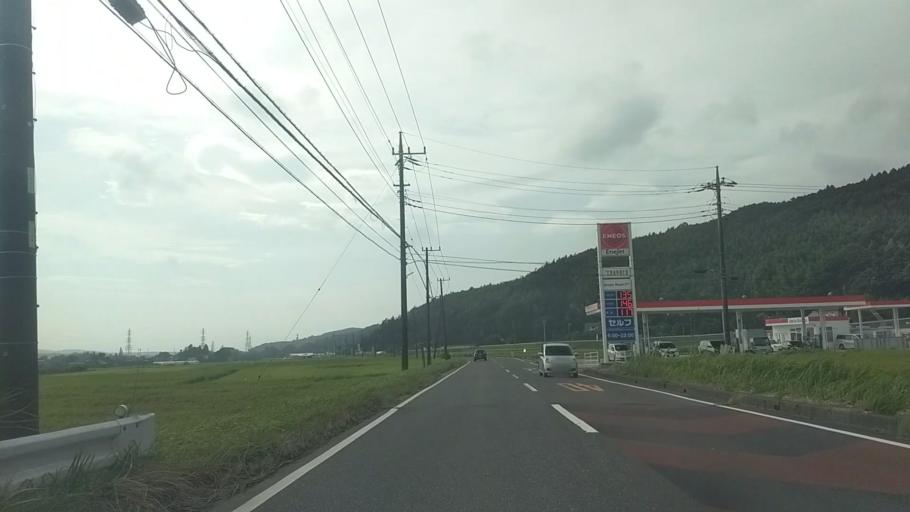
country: JP
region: Chiba
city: Kisarazu
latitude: 35.3087
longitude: 139.9755
